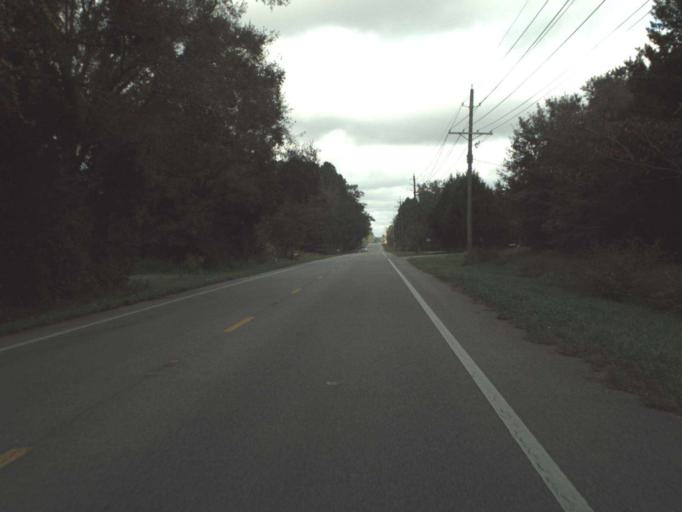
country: US
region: Florida
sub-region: Calhoun County
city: Blountstown
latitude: 30.5010
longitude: -85.1157
